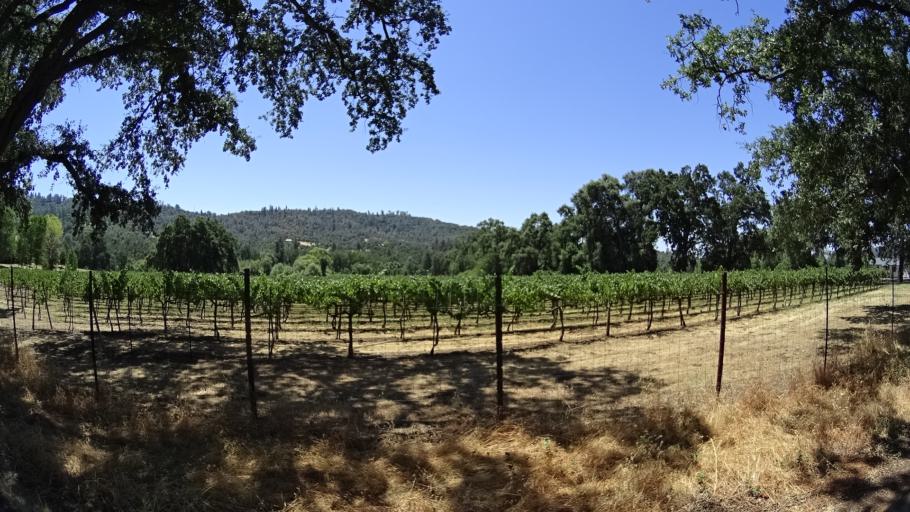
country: US
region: California
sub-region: Calaveras County
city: Murphys
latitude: 38.1304
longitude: -120.4366
